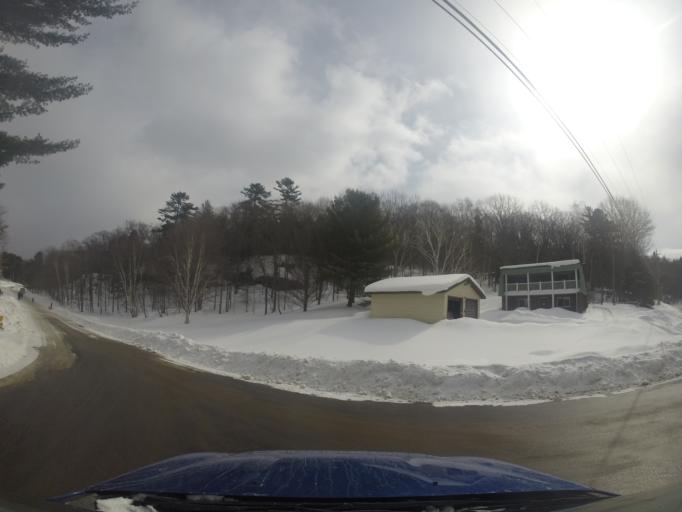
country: CA
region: Ontario
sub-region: Parry Sound District
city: Parry Sound
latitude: 45.3863
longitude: -80.0267
